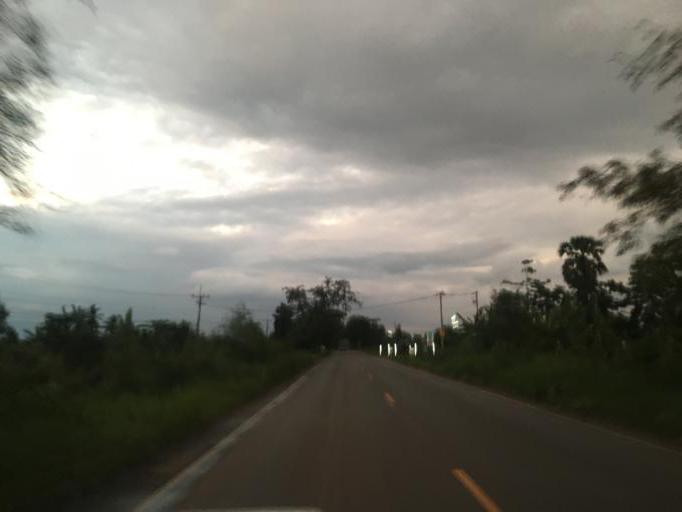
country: TH
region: Changwat Udon Thani
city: Udon Thani
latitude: 17.2950
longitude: 102.7039
